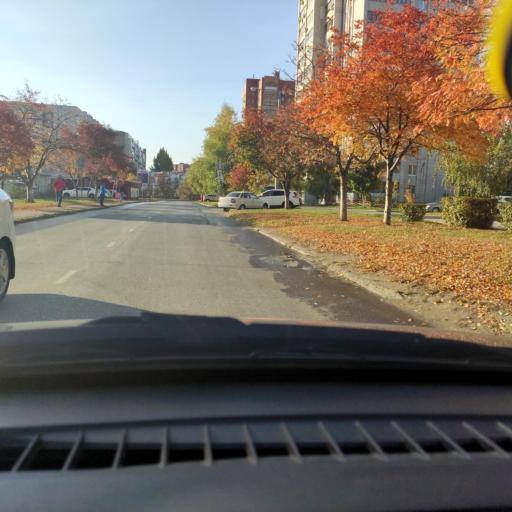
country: RU
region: Samara
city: Tol'yatti
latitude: 53.5419
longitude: 49.3524
